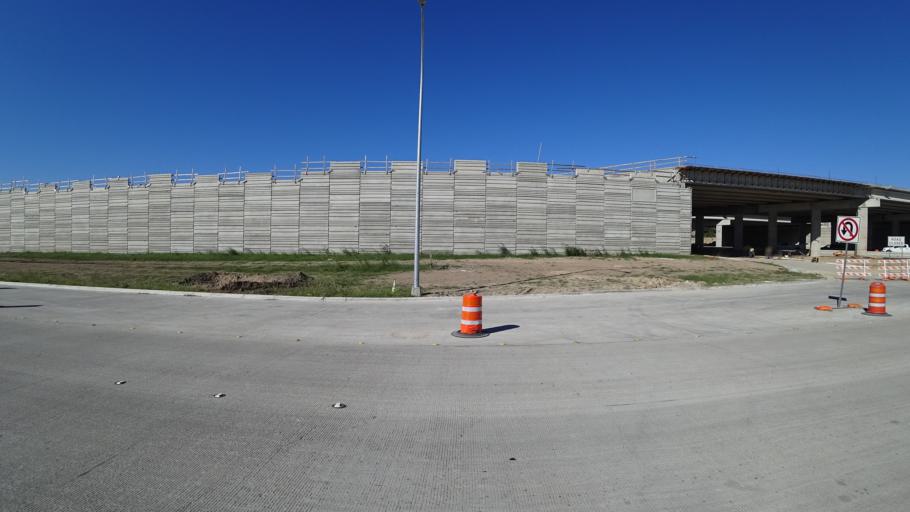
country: US
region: Texas
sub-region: Travis County
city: Austin
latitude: 30.3157
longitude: -97.6623
